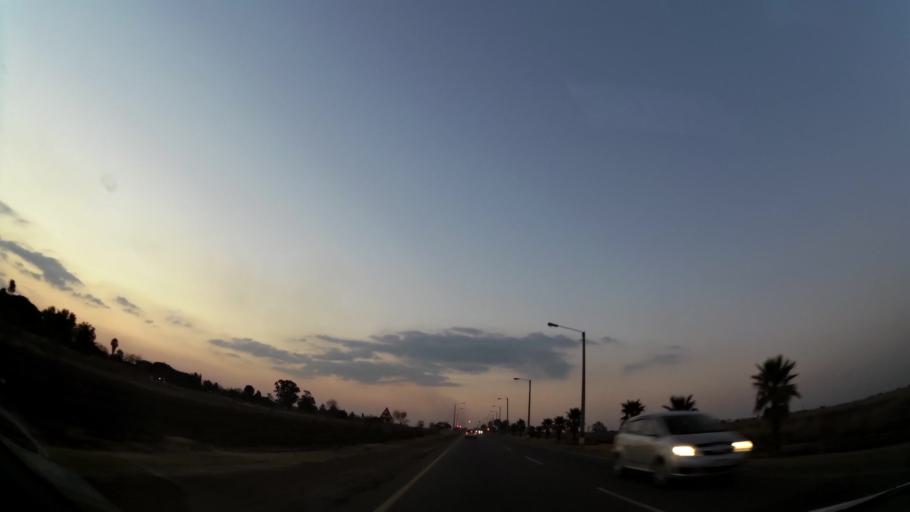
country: ZA
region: Gauteng
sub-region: Ekurhuleni Metropolitan Municipality
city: Springs
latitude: -26.3052
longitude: 28.4550
